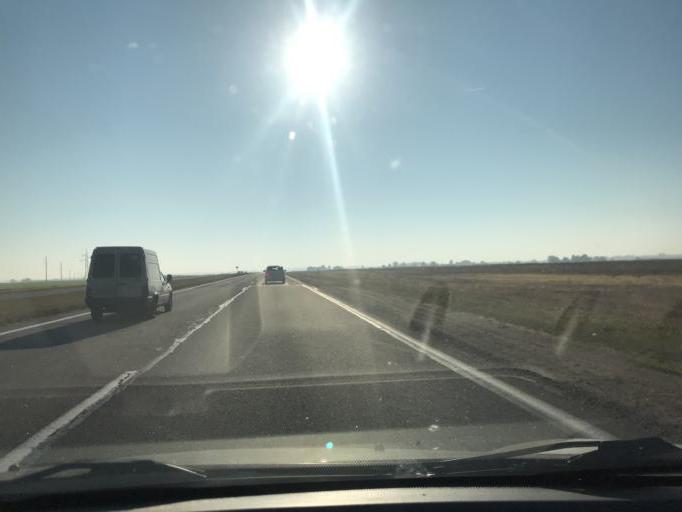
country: BY
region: Minsk
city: Blon'
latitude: 53.5826
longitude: 28.1166
